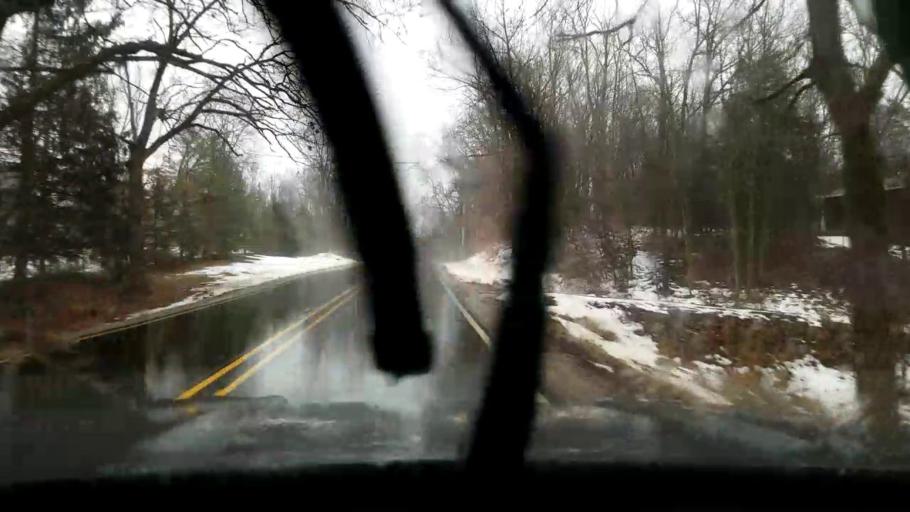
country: US
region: Michigan
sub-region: Jackson County
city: Grass Lake
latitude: 42.3363
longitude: -84.1658
